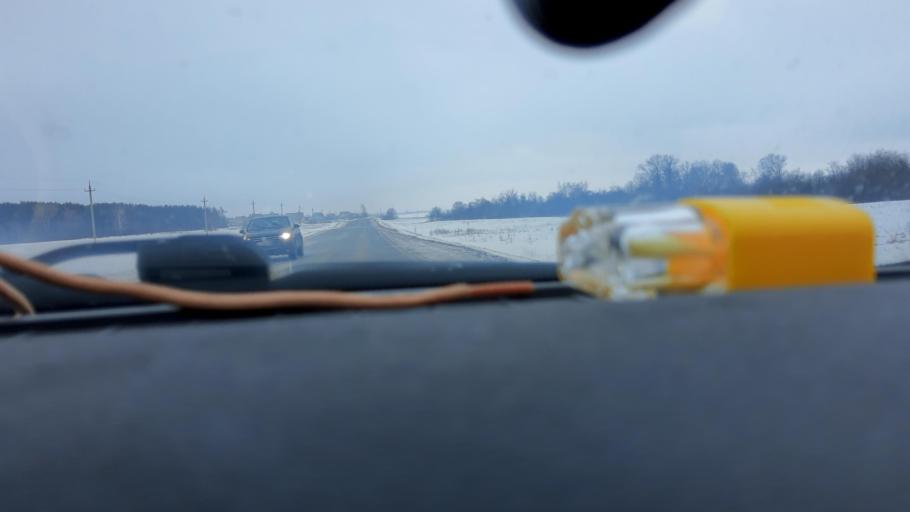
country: RU
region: Bashkortostan
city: Iglino
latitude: 54.7249
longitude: 56.4053
